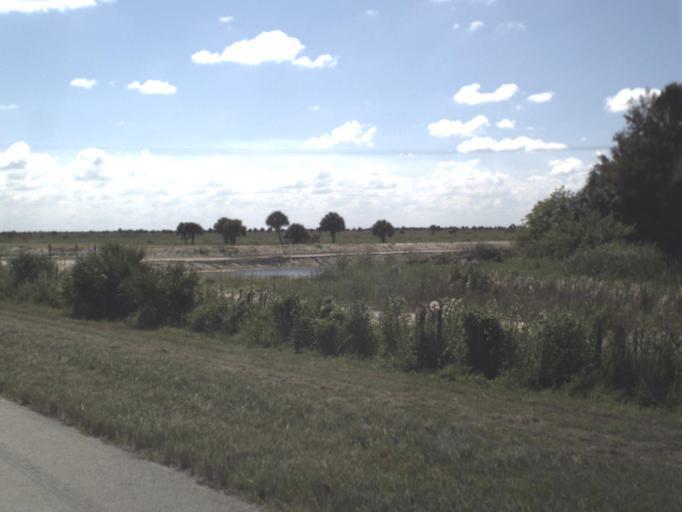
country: US
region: Florida
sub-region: Glades County
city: Moore Haven
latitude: 26.9235
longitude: -81.1223
